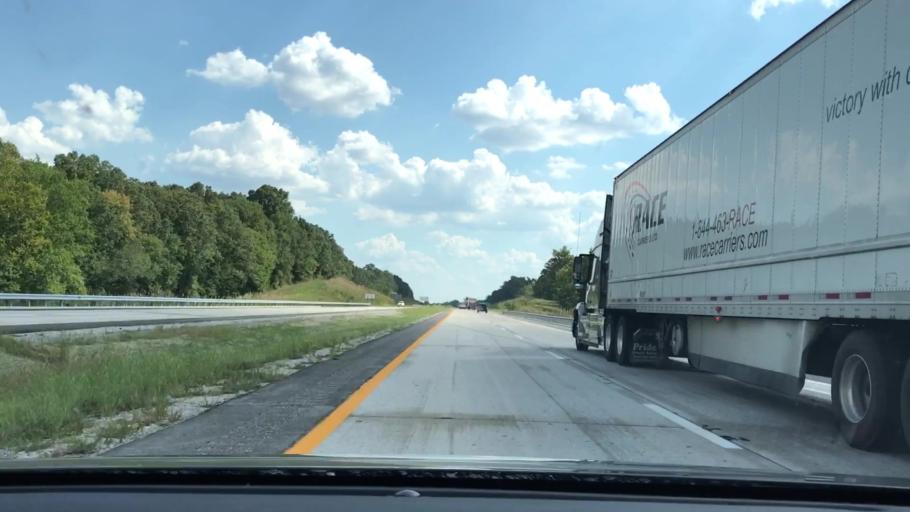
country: US
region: Kentucky
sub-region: Ohio County
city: Oak Grove
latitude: 37.3780
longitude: -86.8054
